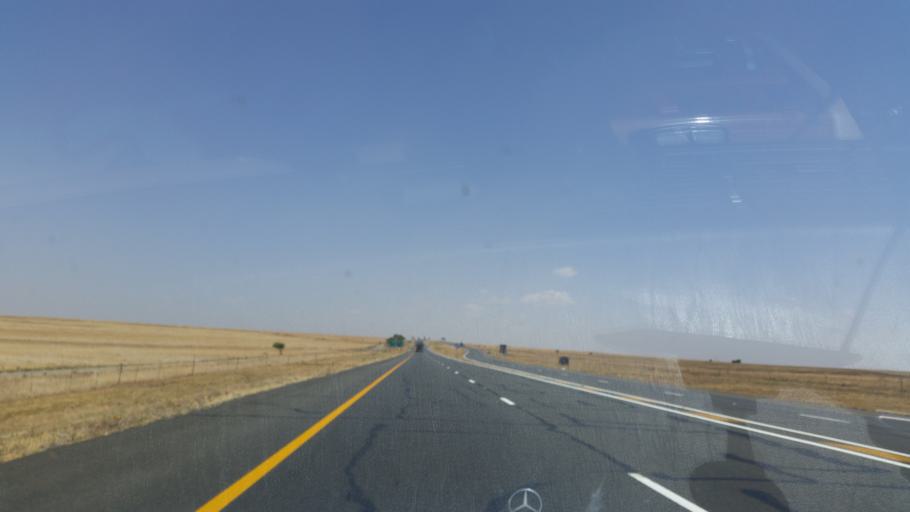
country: ZA
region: Orange Free State
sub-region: Lejweleputswa District Municipality
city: Brandfort
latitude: -28.8786
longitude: 26.5037
